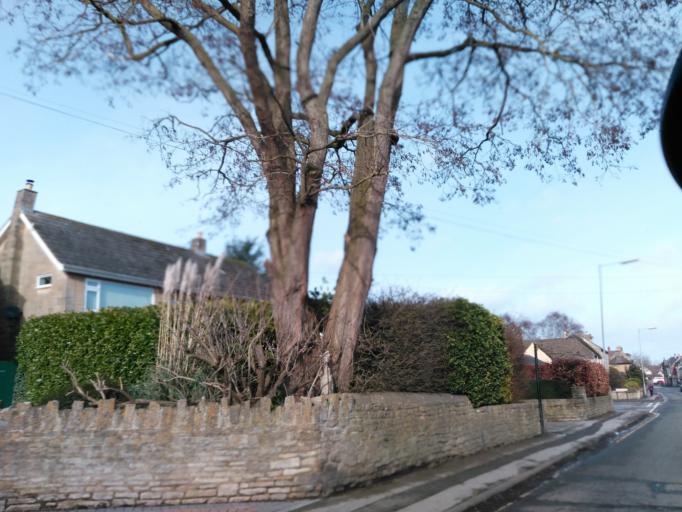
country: GB
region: England
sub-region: Wiltshire
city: Melksham
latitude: 51.3690
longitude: -2.1387
